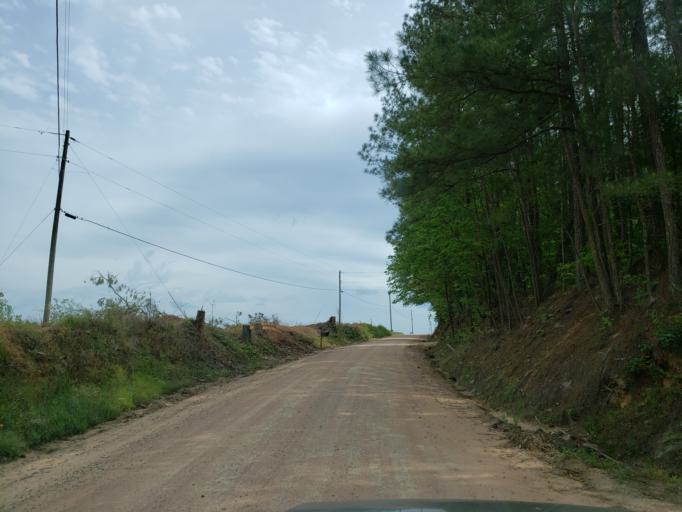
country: US
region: Georgia
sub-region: Monroe County
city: Forsyth
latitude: 32.9824
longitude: -83.9136
